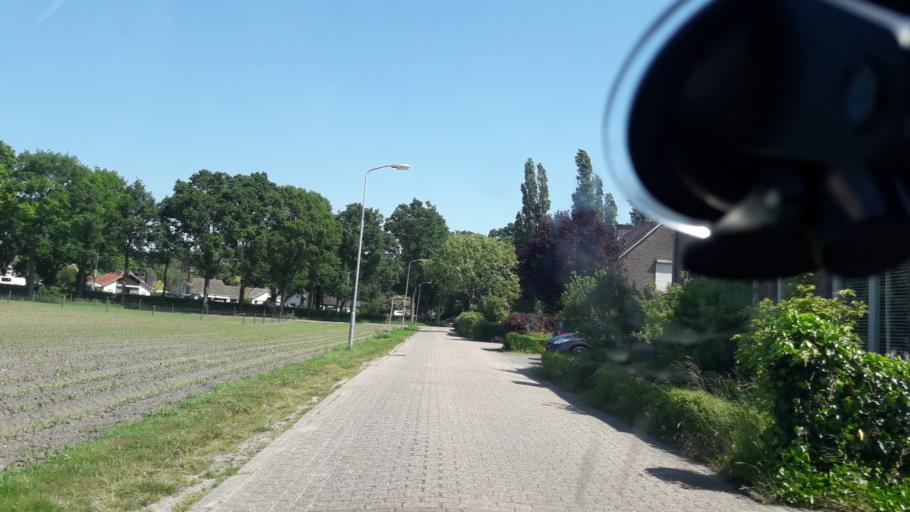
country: NL
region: Overijssel
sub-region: Gemeente Deventer
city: Deventer
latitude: 52.2449
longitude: 6.1471
